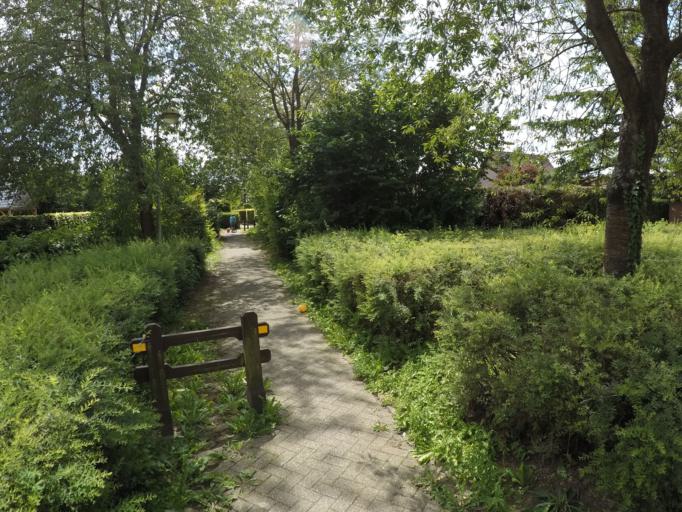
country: BE
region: Flanders
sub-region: Provincie Antwerpen
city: Ranst
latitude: 51.1821
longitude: 4.5634
